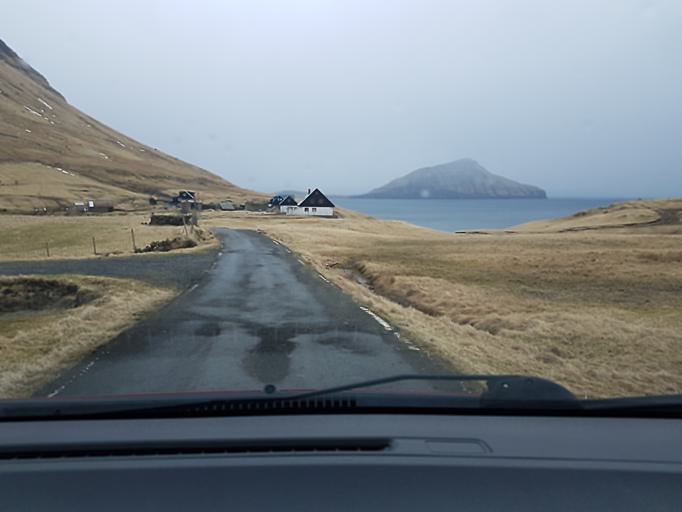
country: FO
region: Streymoy
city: Kollafjordhur
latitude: 62.0420
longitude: -6.9260
